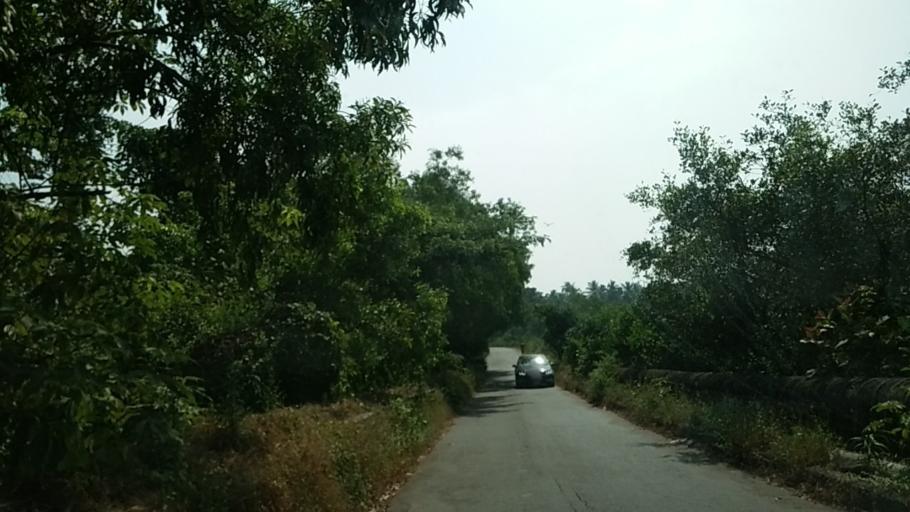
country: IN
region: Goa
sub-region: North Goa
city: Goa Velha
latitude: 15.4424
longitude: 73.8672
